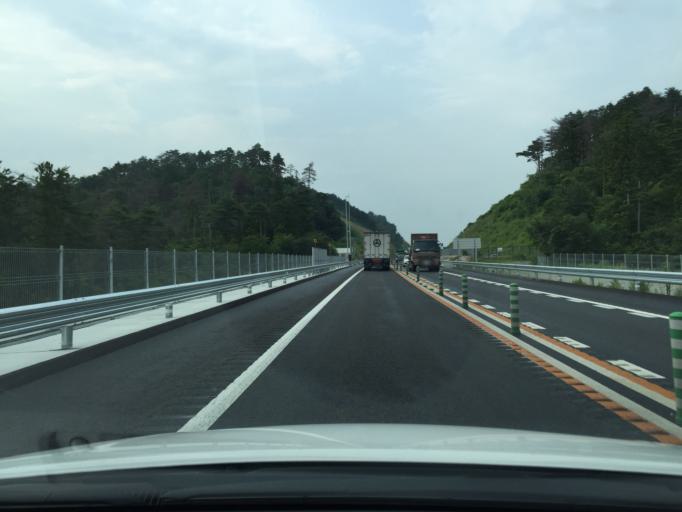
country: JP
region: Fukushima
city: Namie
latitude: 37.4355
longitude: 140.9586
